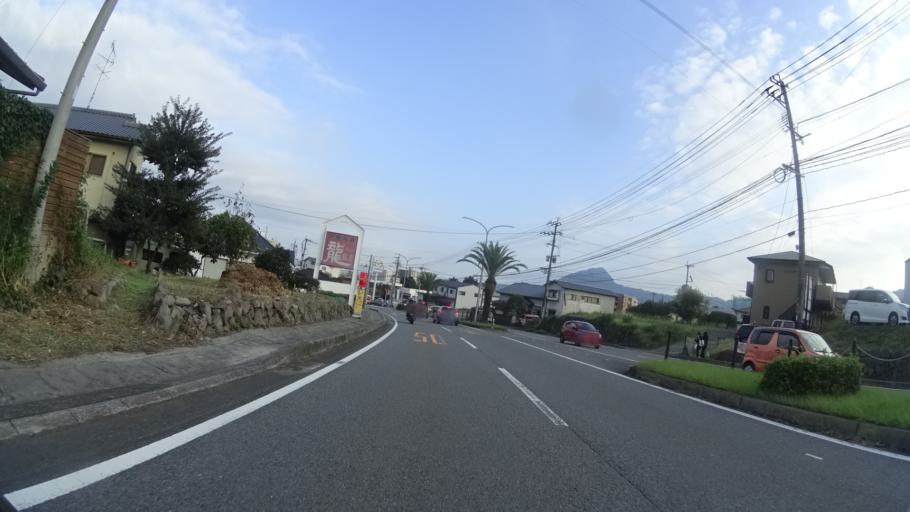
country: JP
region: Oita
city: Beppu
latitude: 33.3060
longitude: 131.4892
